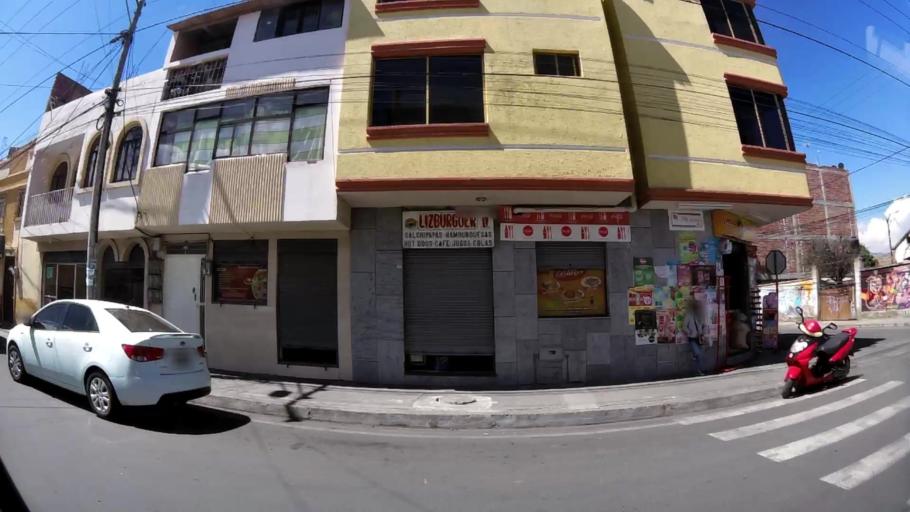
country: EC
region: Chimborazo
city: Riobamba
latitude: -1.6784
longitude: -78.6435
